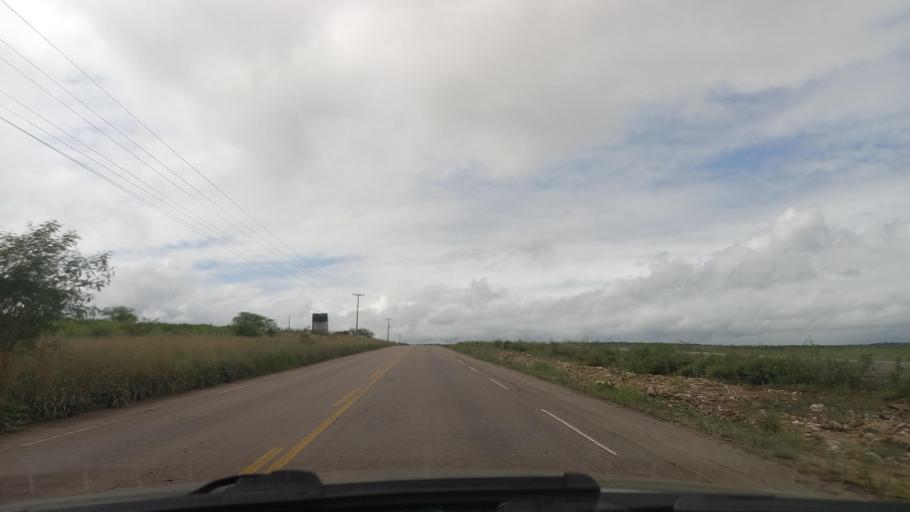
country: BR
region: Alagoas
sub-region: Batalha
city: Batalha
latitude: -9.6533
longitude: -37.1805
